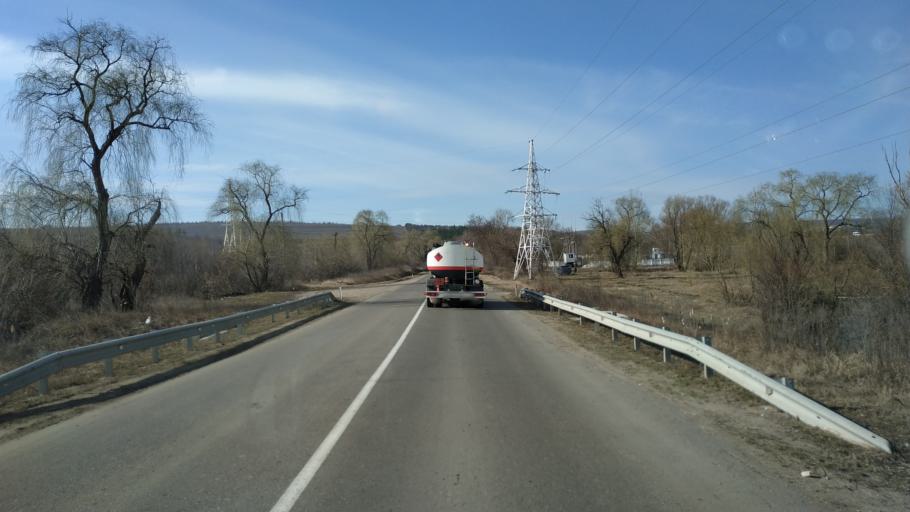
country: MD
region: Laloveni
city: Ialoveni
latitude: 46.9544
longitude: 28.7468
